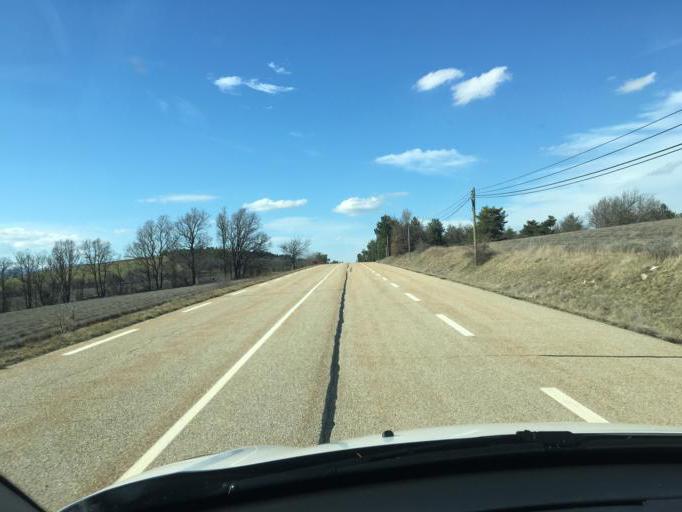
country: FR
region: Provence-Alpes-Cote d'Azur
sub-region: Departement du Vaucluse
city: Sault
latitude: 44.0256
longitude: 5.4679
